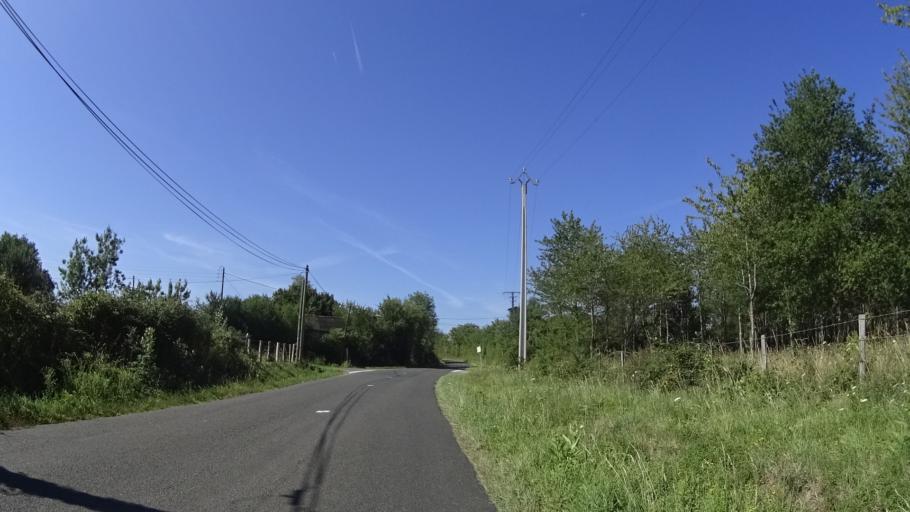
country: FR
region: Pays de la Loire
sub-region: Departement de Maine-et-Loire
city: Soulaire-et-Bourg
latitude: 47.6043
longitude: -0.5221
